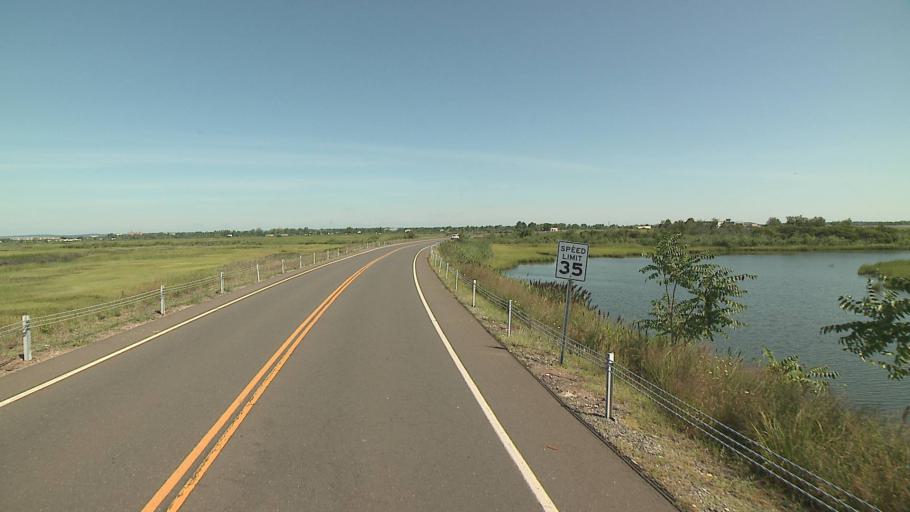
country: US
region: Connecticut
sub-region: Fairfield County
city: Stratford
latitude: 41.1564
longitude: -73.1345
